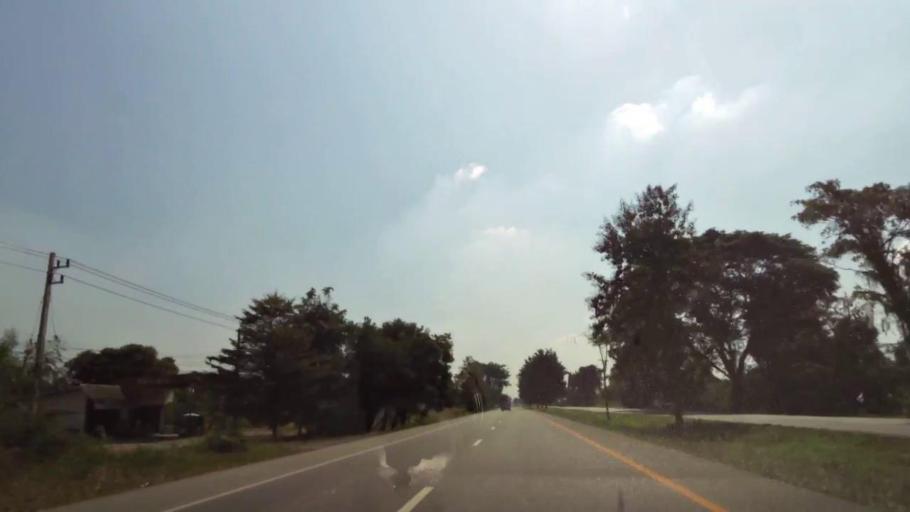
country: TH
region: Phichit
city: Bueng Na Rang
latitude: 16.2314
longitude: 100.1258
